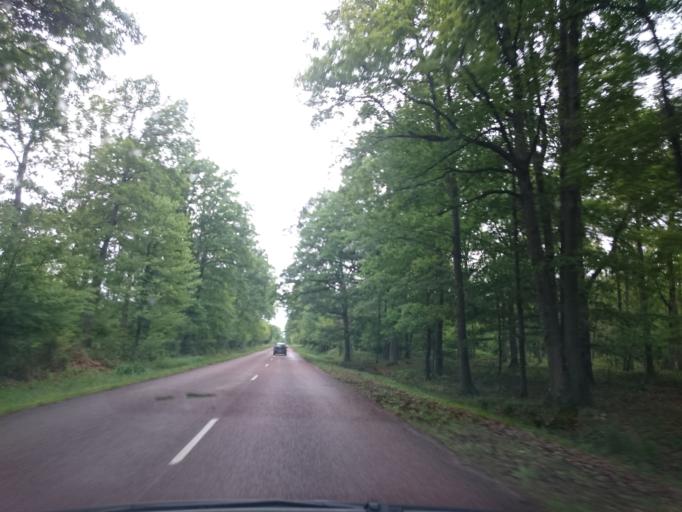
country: FR
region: Centre
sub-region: Departement du Loir-et-Cher
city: Saint-Dye-sur-Loire
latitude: 47.6299
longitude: 1.5142
